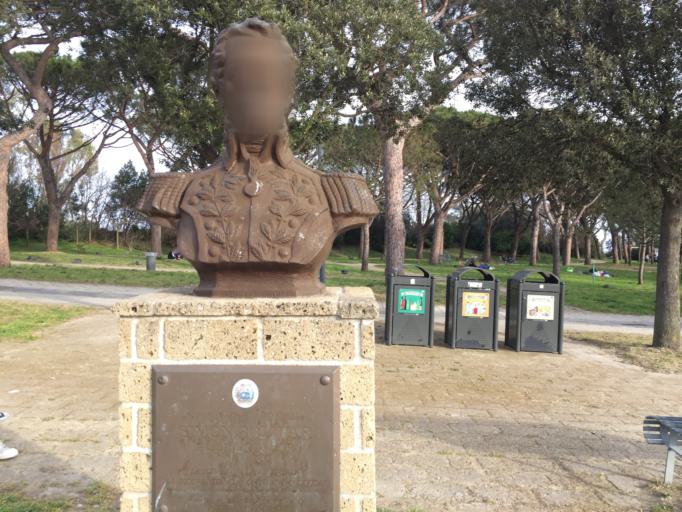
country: IT
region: Campania
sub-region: Provincia di Napoli
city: Bagnoli
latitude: 40.7988
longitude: 14.1769
